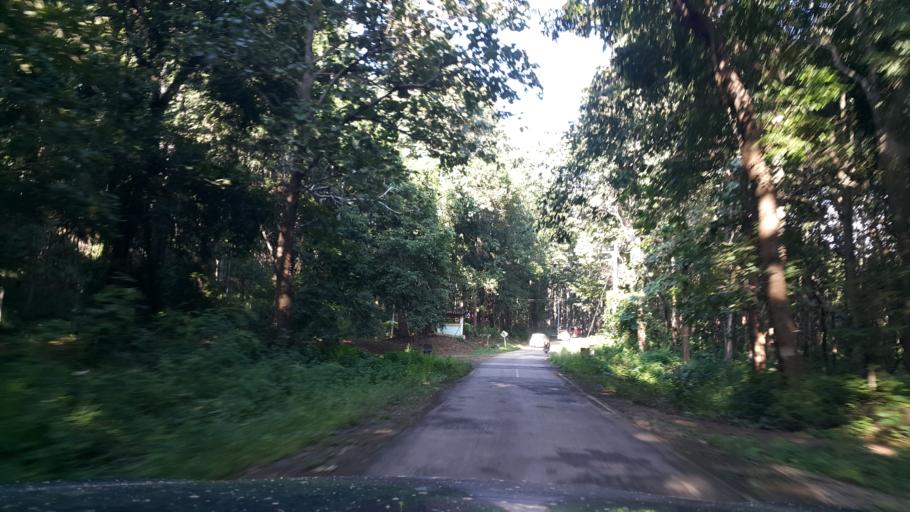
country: TH
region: Chiang Mai
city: Mae Taeng
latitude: 19.0731
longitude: 99.0849
